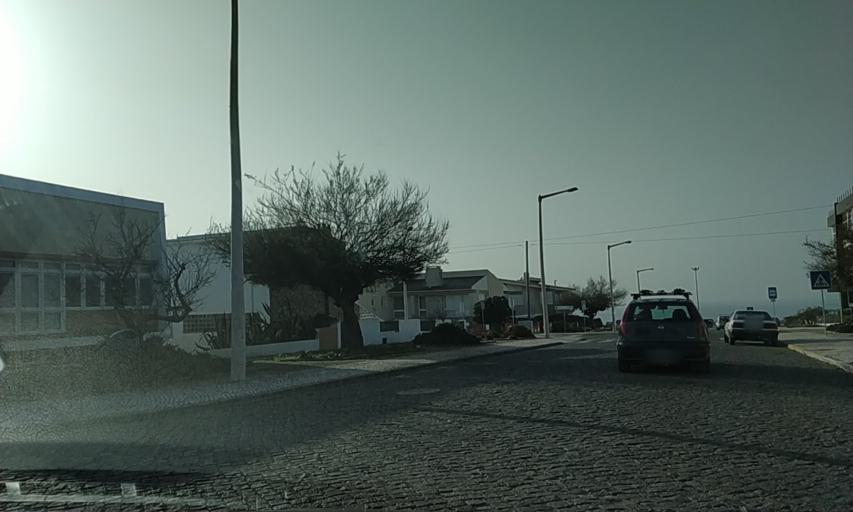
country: PT
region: Leiria
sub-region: Alcobaca
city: Pataias
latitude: 39.7586
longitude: -9.0310
